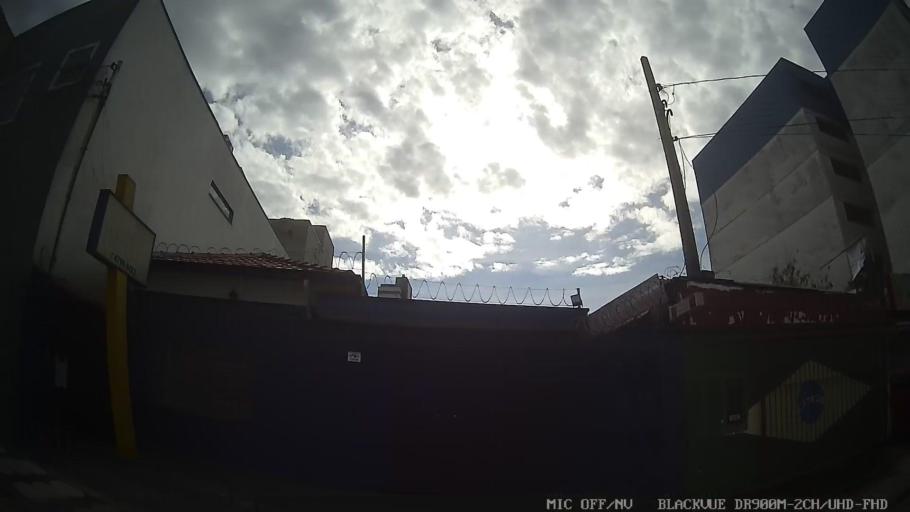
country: BR
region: Sao Paulo
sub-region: Mogi das Cruzes
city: Mogi das Cruzes
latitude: -23.5265
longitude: -46.1961
